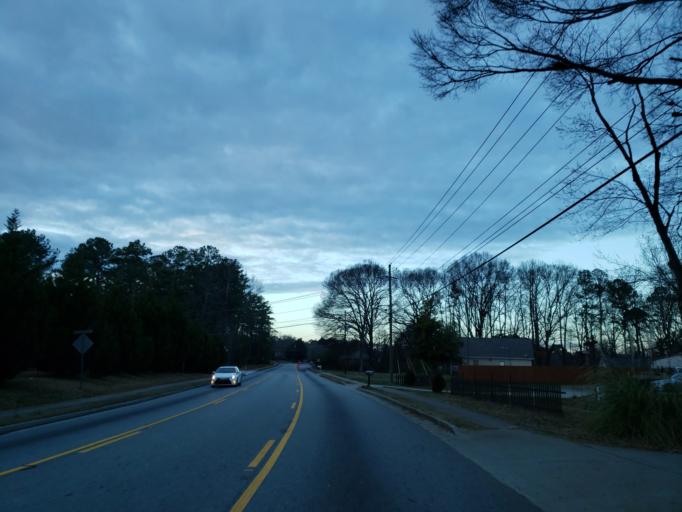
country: US
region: Georgia
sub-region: Cobb County
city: Mableton
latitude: 33.8481
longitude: -84.5859
